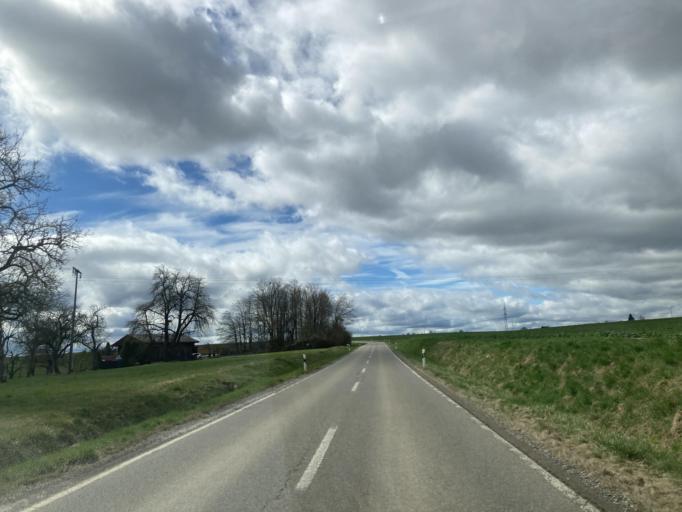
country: DE
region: Baden-Wuerttemberg
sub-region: Tuebingen Region
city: Rottenburg
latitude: 48.4780
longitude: 8.8805
